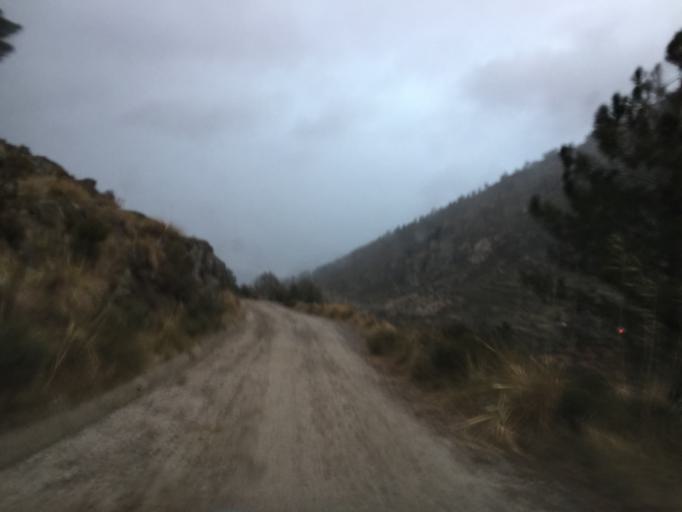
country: PT
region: Guarda
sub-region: Manteigas
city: Manteigas
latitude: 40.3703
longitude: -7.5517
